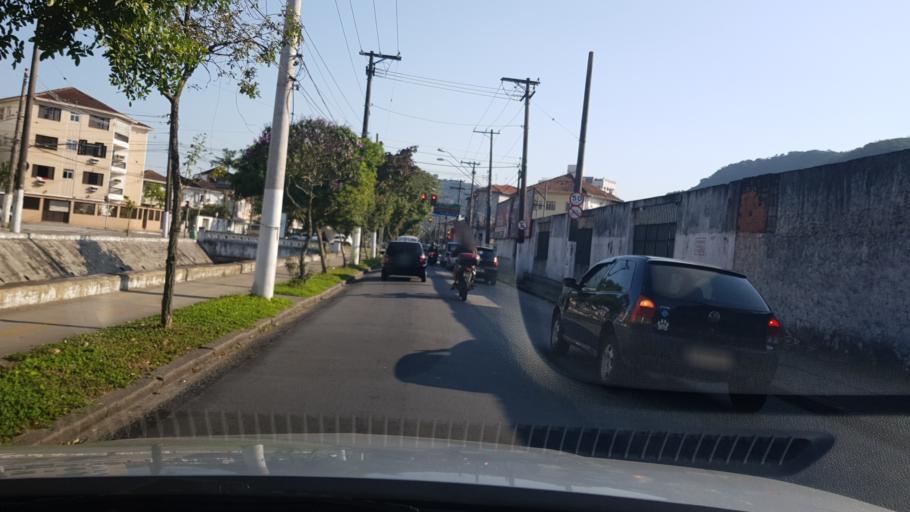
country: BR
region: Sao Paulo
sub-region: Santos
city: Santos
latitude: -23.9479
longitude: -46.3376
